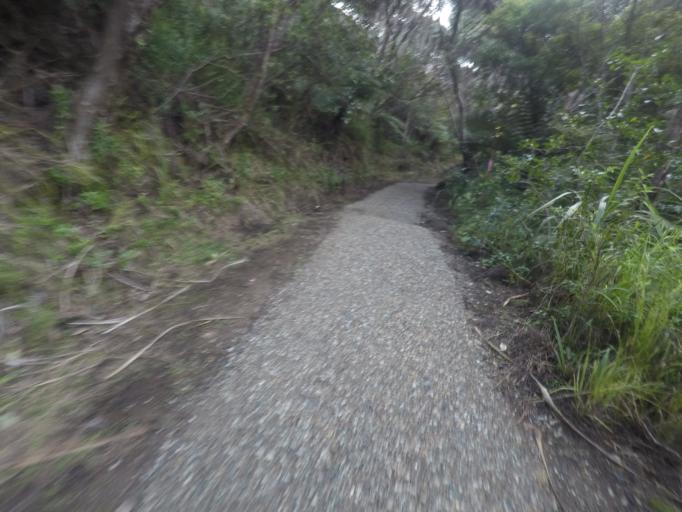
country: NZ
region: Auckland
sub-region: Auckland
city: Muriwai Beach
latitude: -36.9809
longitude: 174.4743
